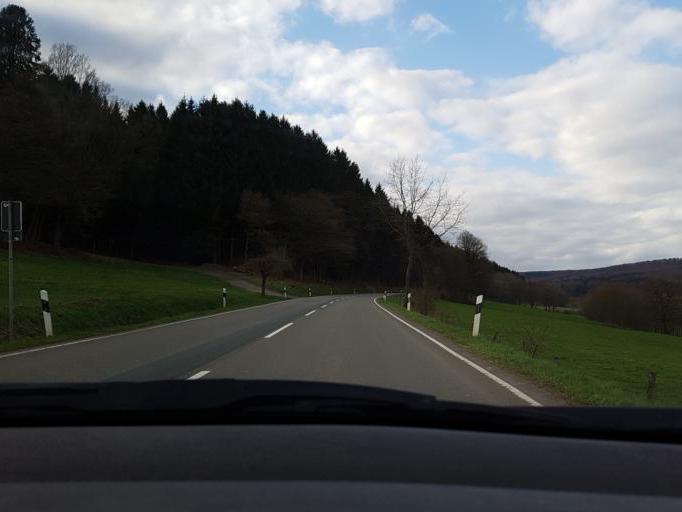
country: DE
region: Lower Saxony
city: Bodenfelde
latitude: 51.6984
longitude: 9.5506
